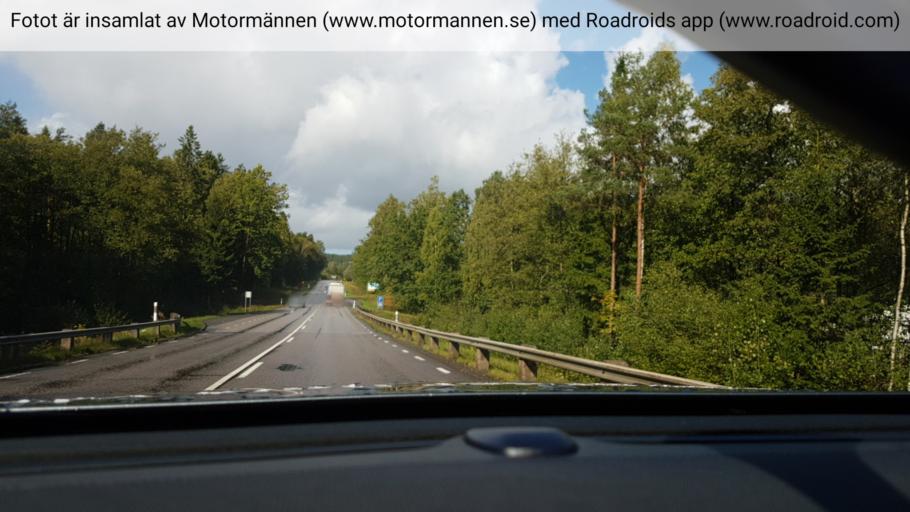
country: SE
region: Vaestra Goetaland
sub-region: Alingsas Kommun
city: Sollebrunn
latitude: 58.0518
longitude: 12.4678
